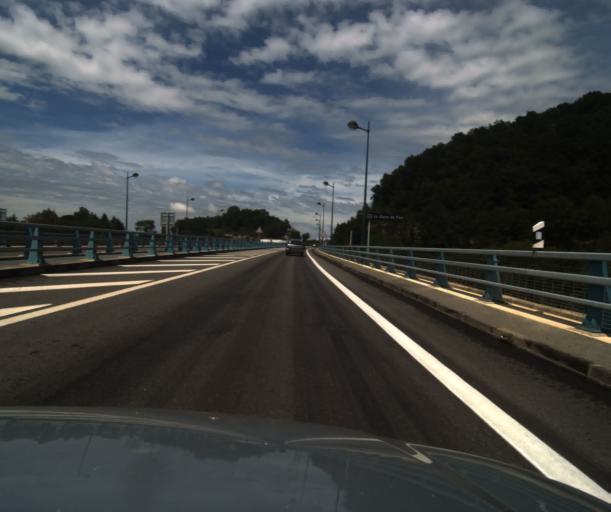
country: FR
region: Midi-Pyrenees
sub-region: Departement des Hautes-Pyrenees
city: Lourdes
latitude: 43.0813
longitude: -0.0447
